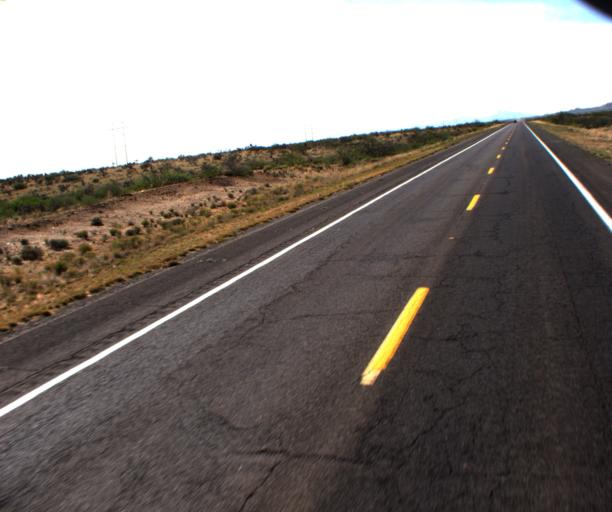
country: US
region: Arizona
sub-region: Graham County
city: Swift Trail Junction
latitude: 32.6148
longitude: -109.6881
